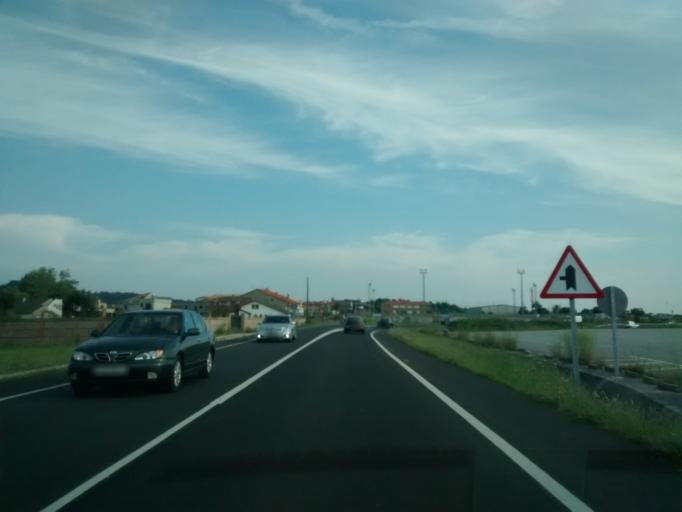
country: ES
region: Galicia
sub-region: Provincia de Pontevedra
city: O Grove
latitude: 42.4417
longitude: -8.8687
